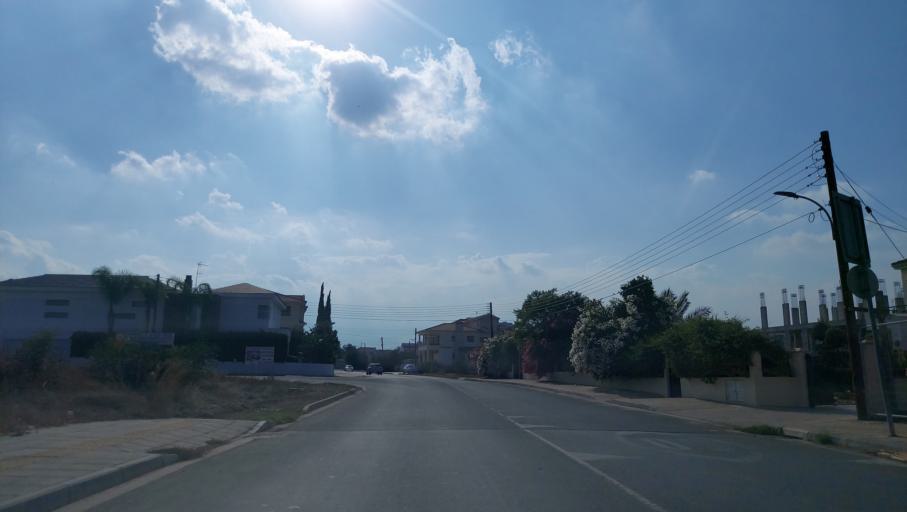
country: CY
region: Lefkosia
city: Tseri
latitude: 35.1065
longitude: 33.3087
